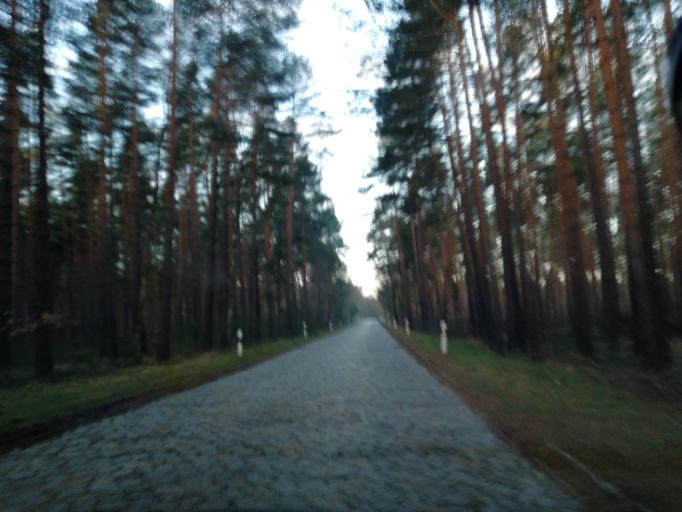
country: DE
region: Brandenburg
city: Bronkow
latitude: 51.7228
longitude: 13.8864
